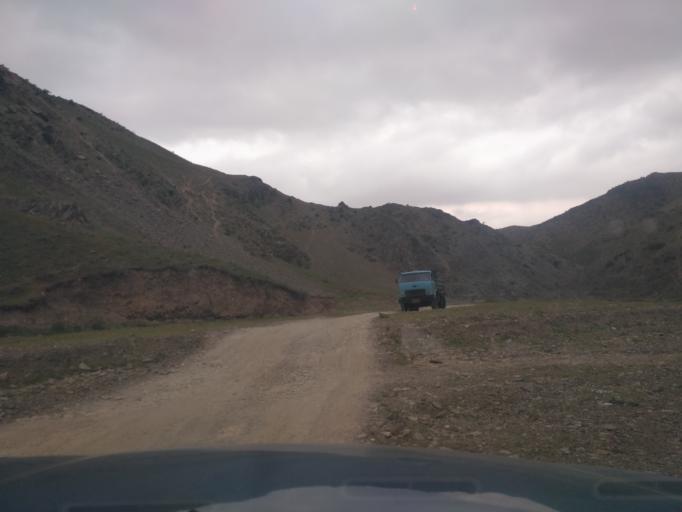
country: UZ
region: Jizzax
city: Zomin
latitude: 39.8503
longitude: 68.3964
